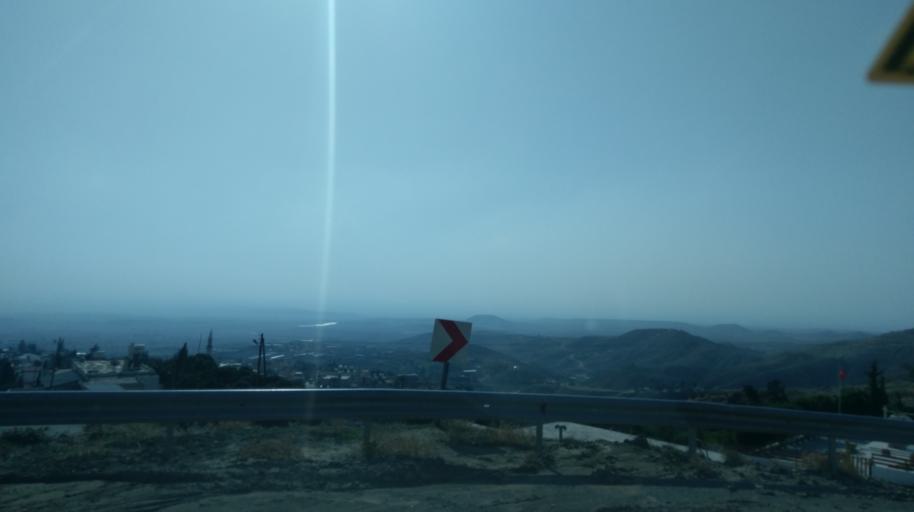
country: CY
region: Ammochostos
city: Lefkonoiko
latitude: 35.2859
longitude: 33.5707
